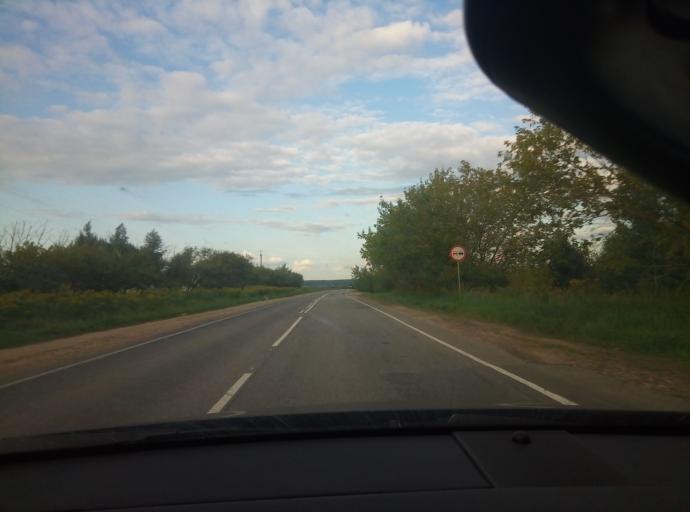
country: RU
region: Tula
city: Leninskiy
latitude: 54.2490
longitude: 37.3301
